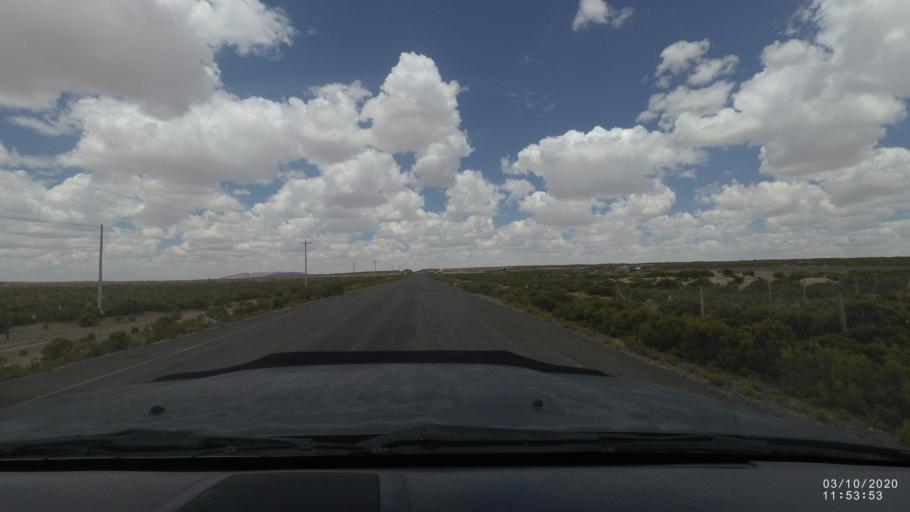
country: BO
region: Oruro
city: Poopo
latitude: -18.4861
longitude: -67.6061
